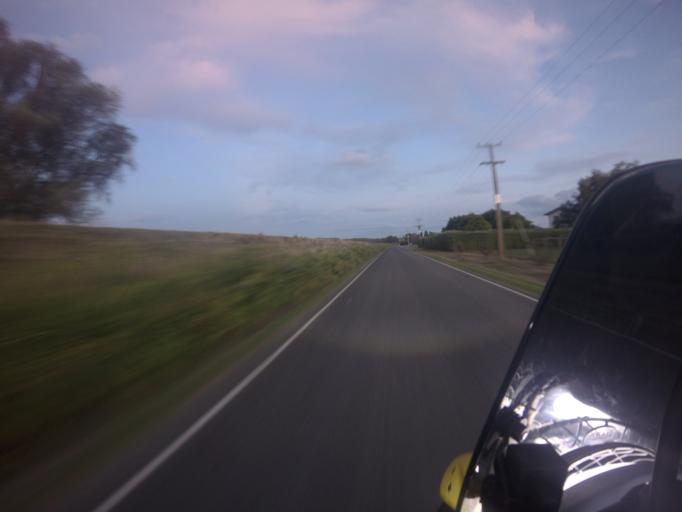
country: NZ
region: Gisborne
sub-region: Gisborne District
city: Gisborne
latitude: -38.6695
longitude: 177.9245
